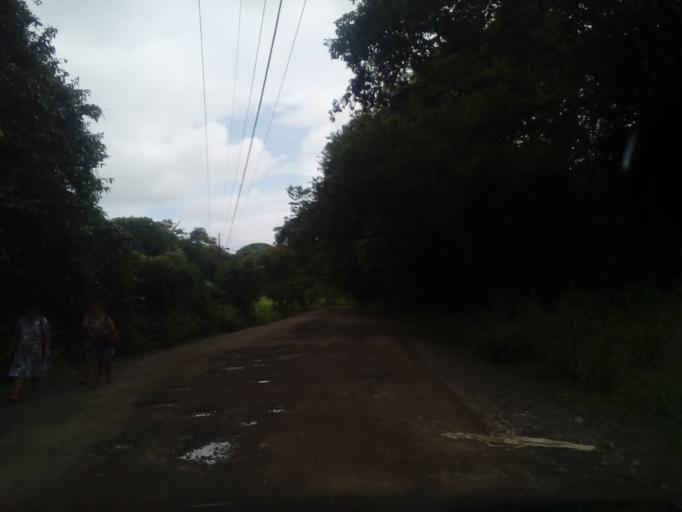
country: CR
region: Guanacaste
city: Samara
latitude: 9.9288
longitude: -85.6539
